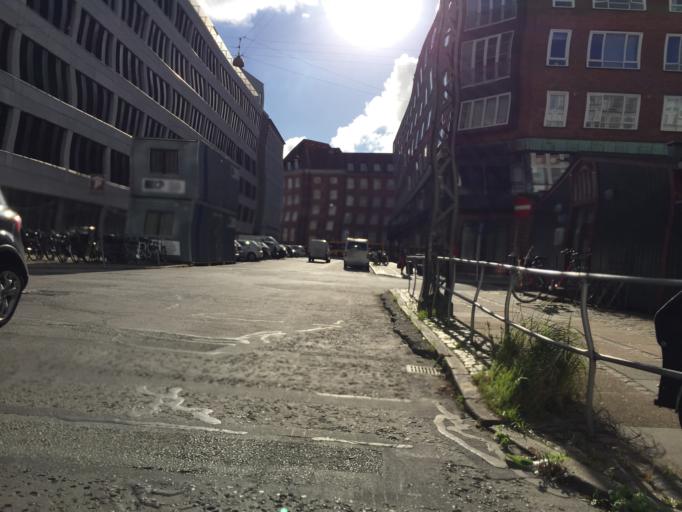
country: DK
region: Capital Region
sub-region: Kobenhavn
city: Copenhagen
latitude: 55.6793
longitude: 12.5610
